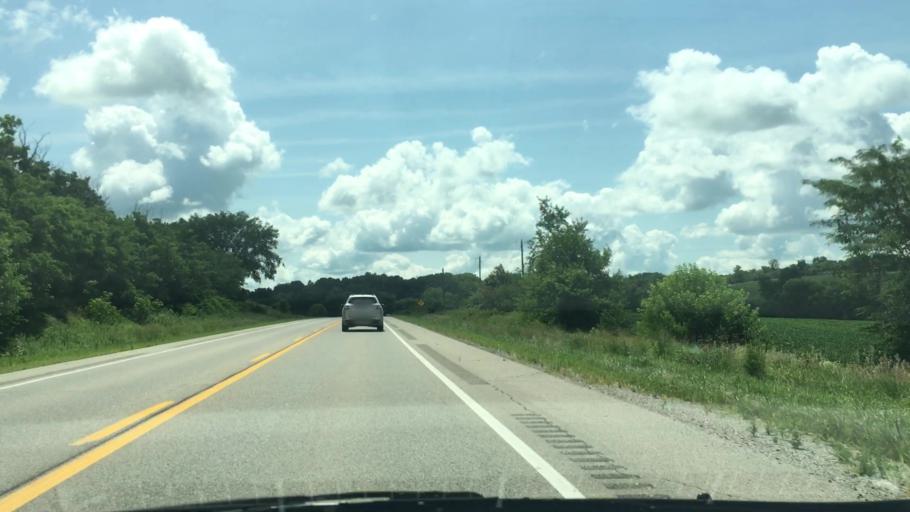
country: US
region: Iowa
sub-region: Johnson County
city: Solon
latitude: 41.7546
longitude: -91.4759
